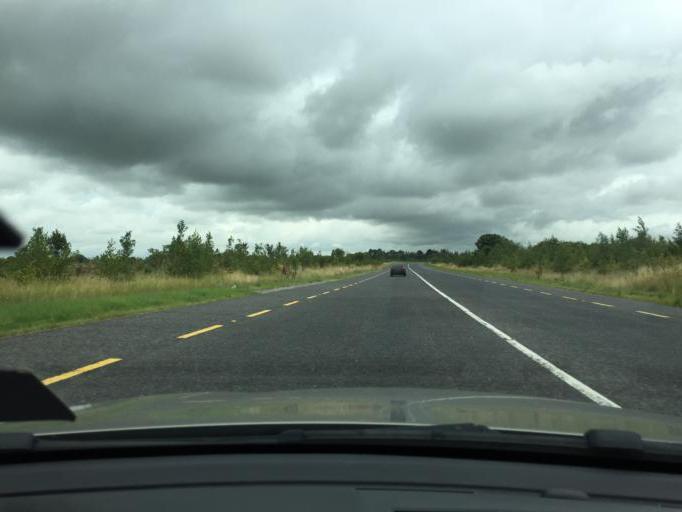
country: IE
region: Leinster
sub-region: An Mhi
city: Dunboyne
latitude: 53.4171
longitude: -6.4912
